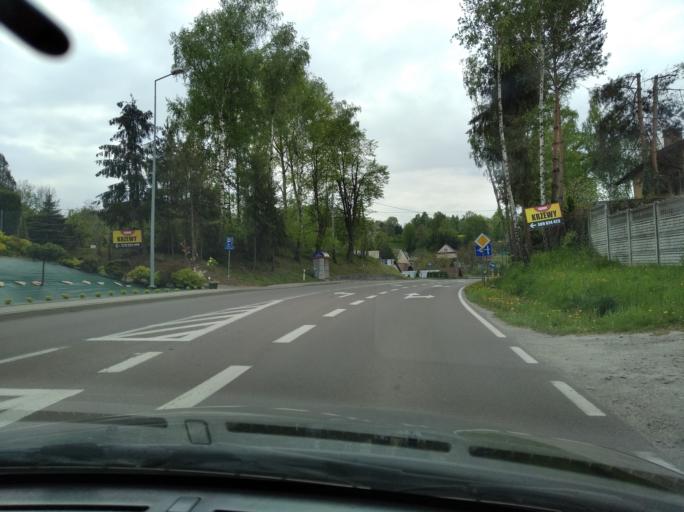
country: PL
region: Lesser Poland Voivodeship
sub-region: Powiat tarnowski
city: Tarnowiec
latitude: 49.9688
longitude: 20.9949
